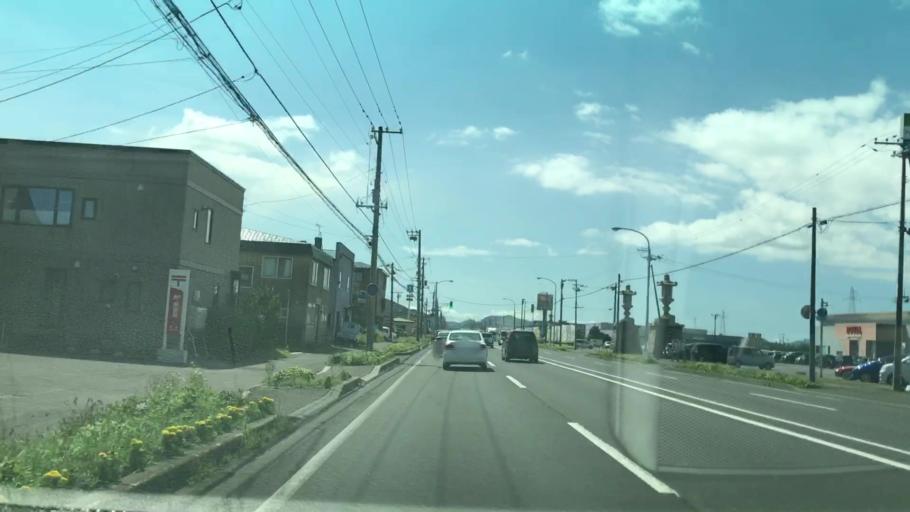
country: JP
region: Hokkaido
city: Muroran
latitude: 42.3723
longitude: 141.0653
